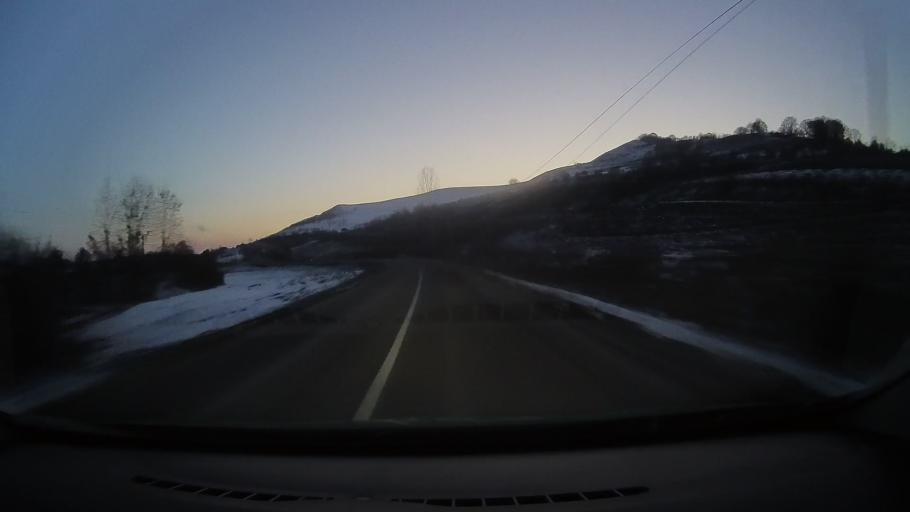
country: RO
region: Sibiu
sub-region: Comuna Alma
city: Alma
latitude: 46.2005
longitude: 24.4472
